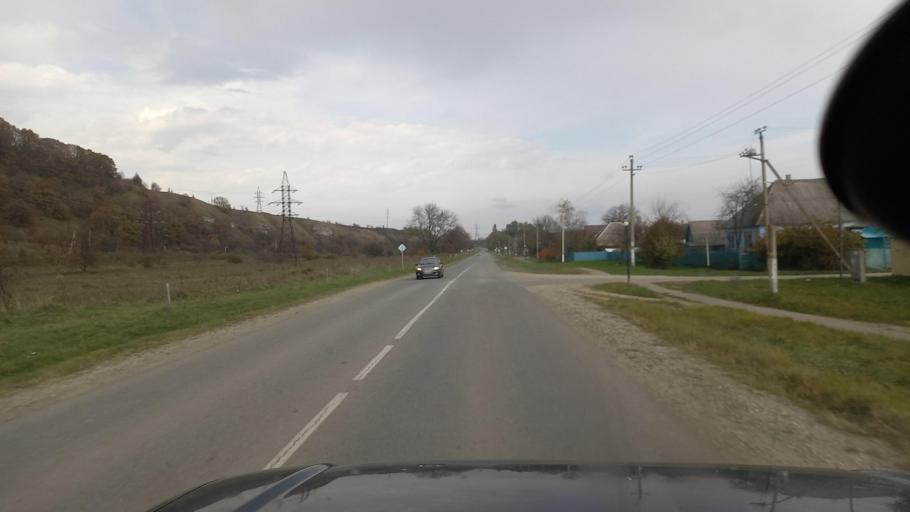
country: RU
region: Krasnodarskiy
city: Psebay
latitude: 44.1572
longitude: 40.8348
